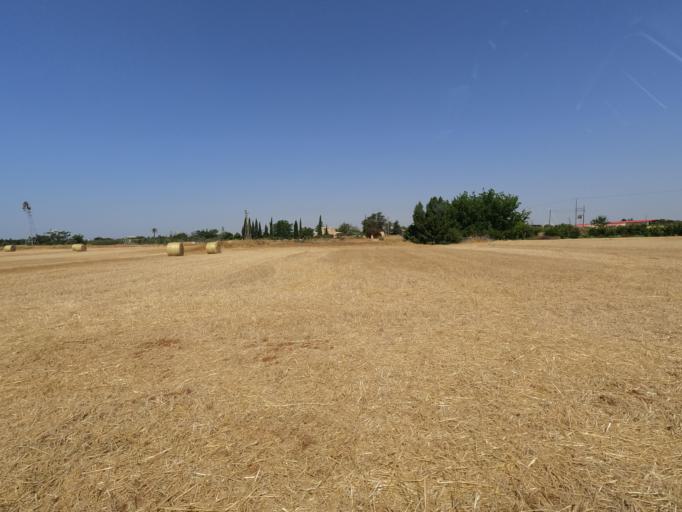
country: CY
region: Ammochostos
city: Frenaros
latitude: 34.9983
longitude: 33.9427
